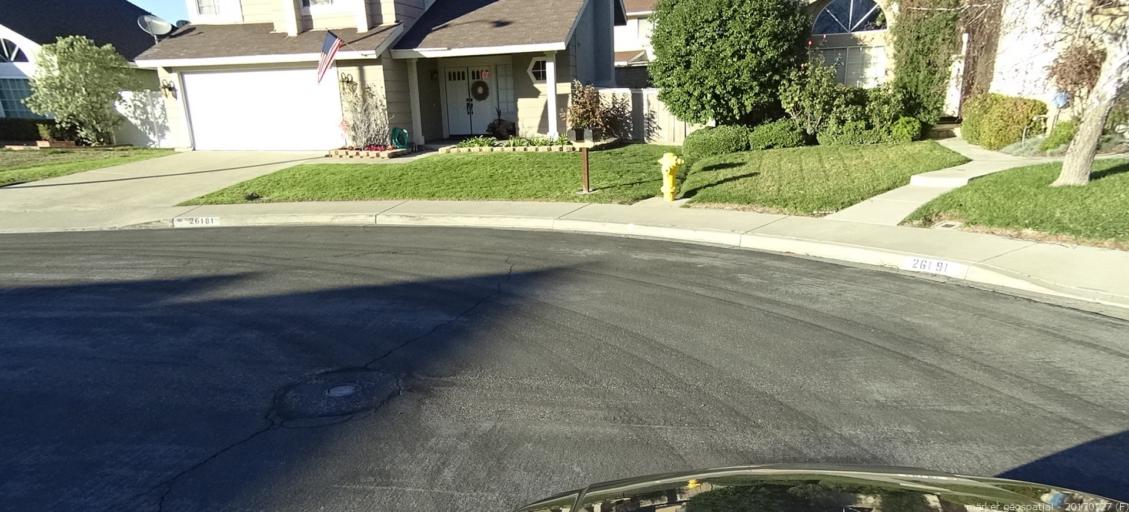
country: US
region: California
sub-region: Orange County
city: Lake Forest
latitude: 33.6558
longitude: -117.6731
